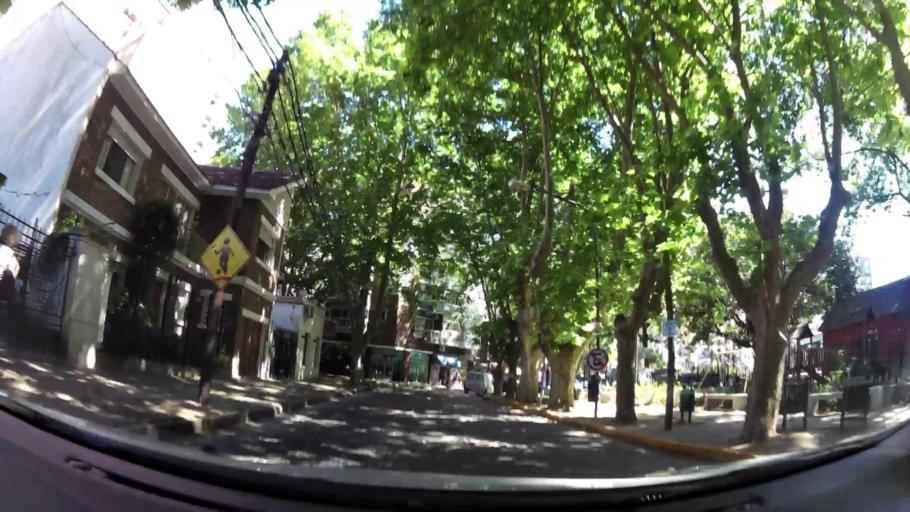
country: AR
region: Buenos Aires
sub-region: Partido de Vicente Lopez
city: Olivos
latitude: -34.5246
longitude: -58.4733
